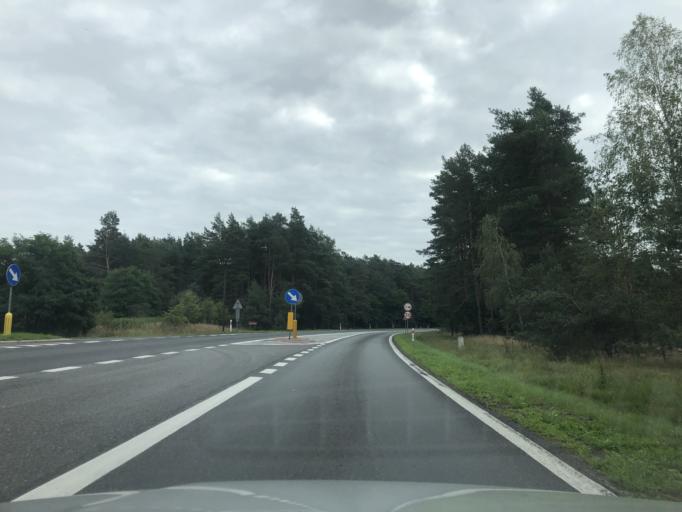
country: PL
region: Greater Poland Voivodeship
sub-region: Powiat pilski
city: Pila
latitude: 53.2281
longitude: 16.7071
